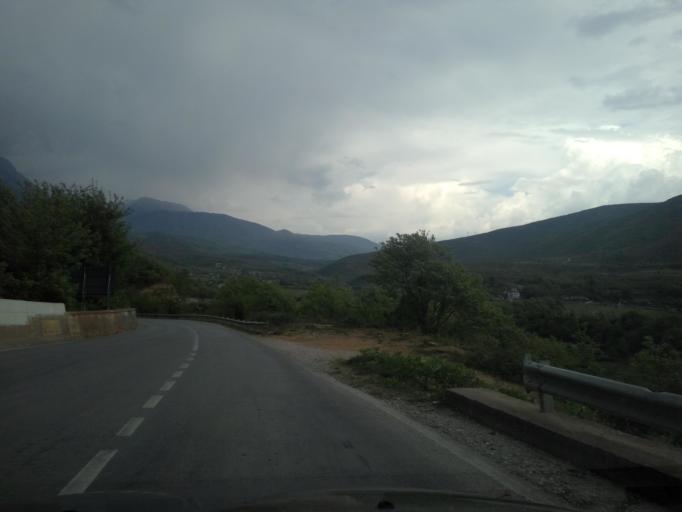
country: AL
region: Kukes
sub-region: Rrethi i Tropojes
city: Llugaj
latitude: 42.3626
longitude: 20.1108
